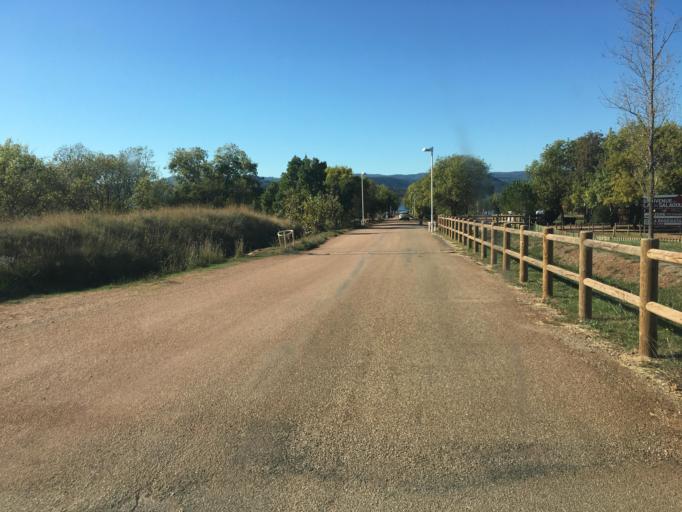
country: FR
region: Languedoc-Roussillon
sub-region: Departement de l'Herault
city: Nebian
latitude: 43.6448
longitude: 3.3899
